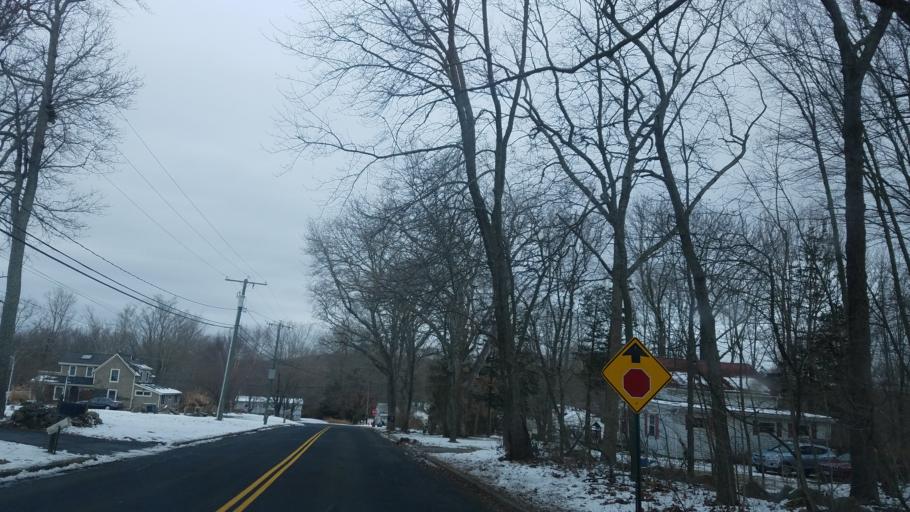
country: US
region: Connecticut
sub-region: New London County
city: Central Waterford
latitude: 41.3462
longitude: -72.1554
